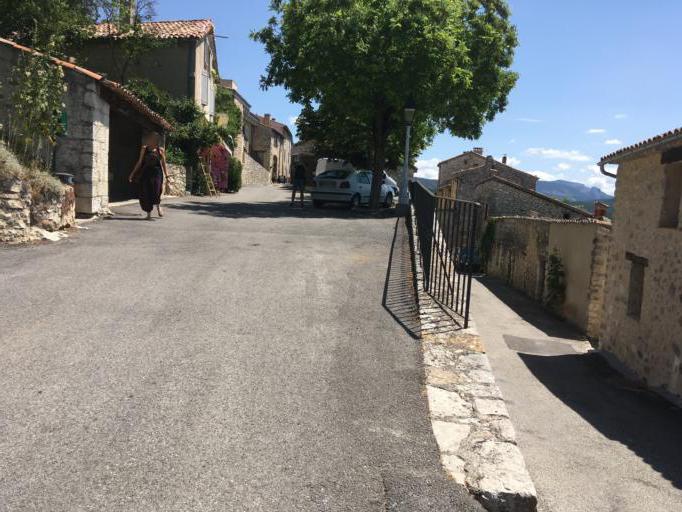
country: FR
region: Provence-Alpes-Cote d'Azur
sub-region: Departement des Alpes-de-Haute-Provence
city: Castellane
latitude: 43.7609
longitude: 6.4434
